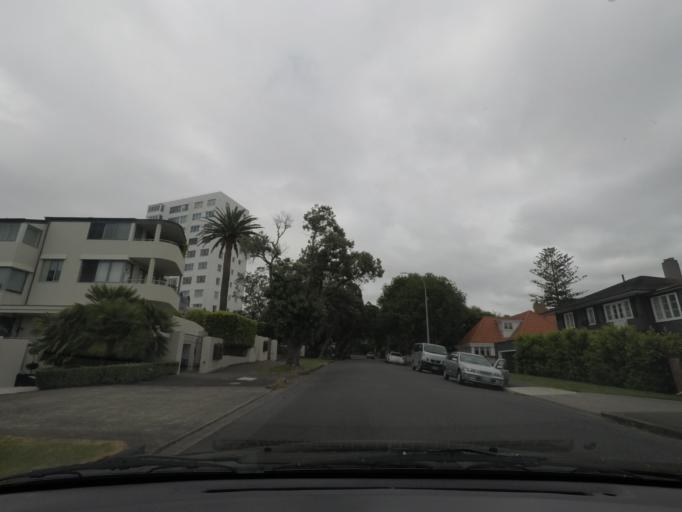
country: NZ
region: Auckland
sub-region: Auckland
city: Auckland
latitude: -36.8511
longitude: 174.7912
